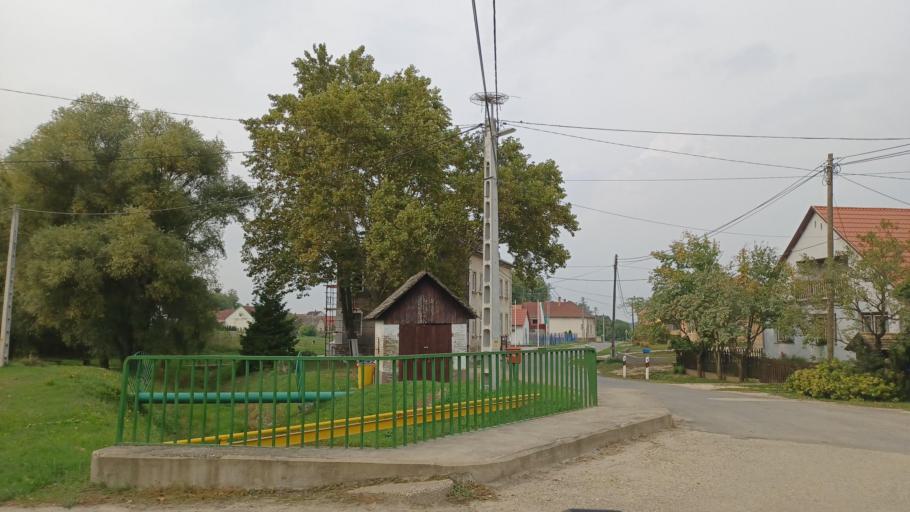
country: HU
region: Tolna
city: Gyonk
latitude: 46.5725
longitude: 18.4255
